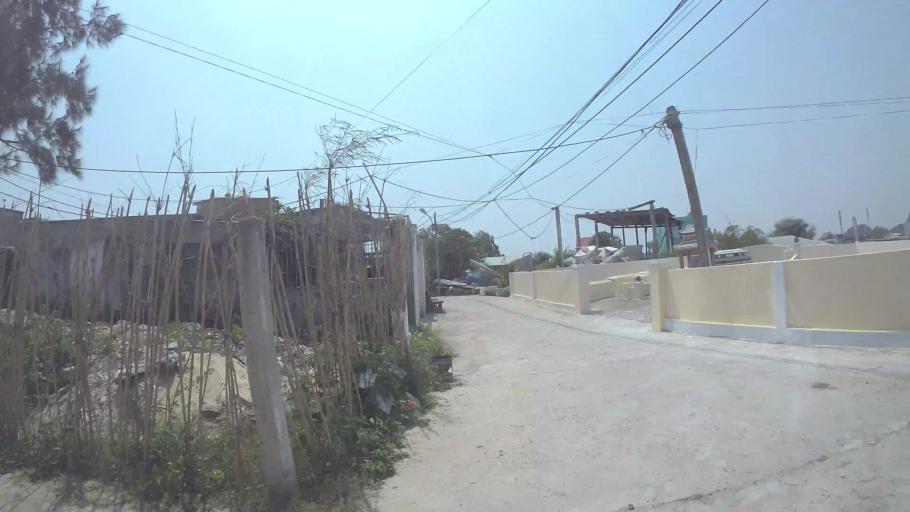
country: VN
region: Da Nang
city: Ngu Hanh Son
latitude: 15.9962
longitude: 108.2654
